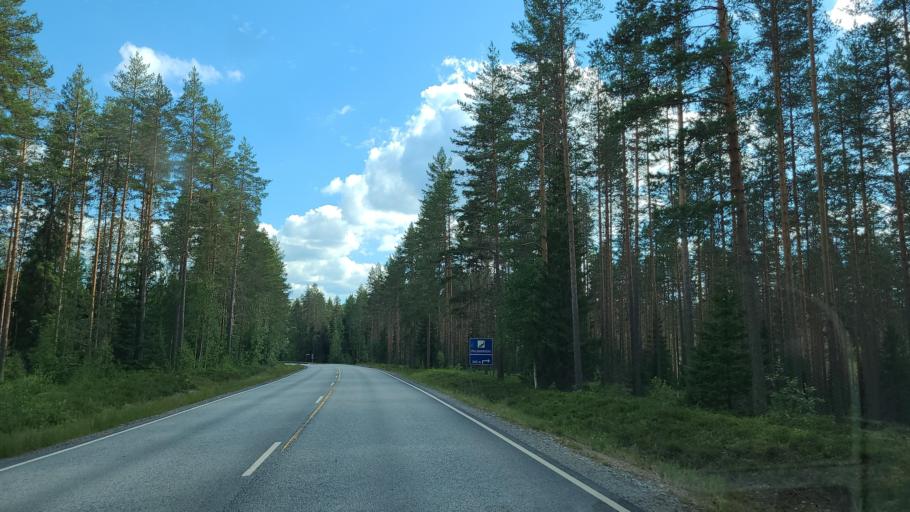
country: FI
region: Central Finland
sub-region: Keuruu
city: Multia
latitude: 62.4916
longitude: 24.6907
